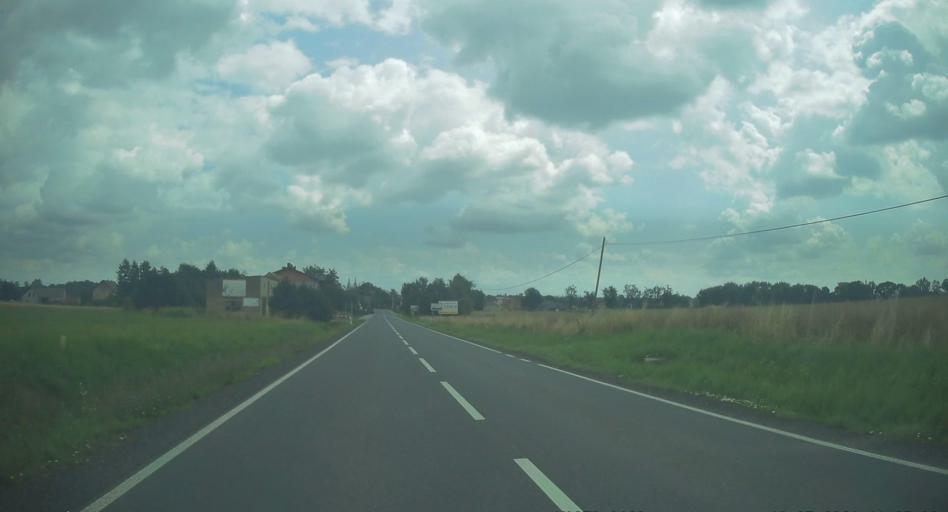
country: PL
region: Opole Voivodeship
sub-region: Powiat prudnicki
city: Glogowek
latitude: 50.3528
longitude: 17.8411
